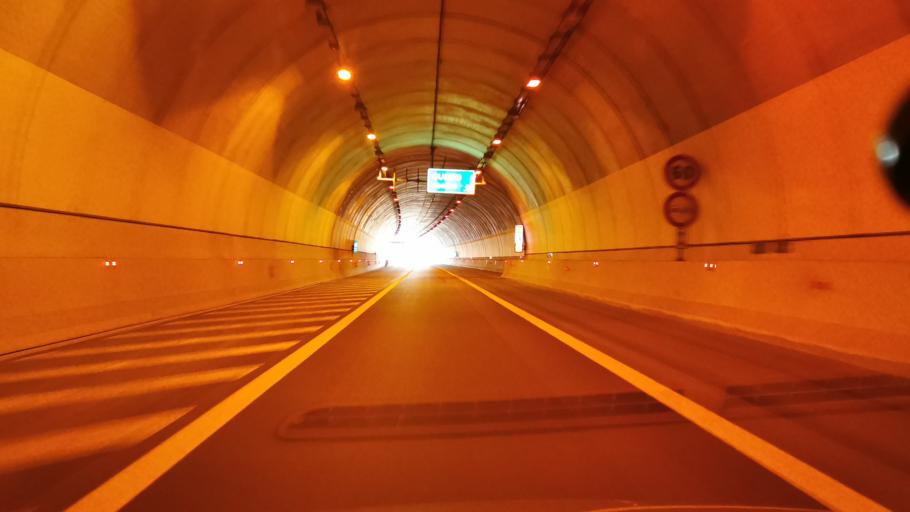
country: IT
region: Piedmont
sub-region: Provincia di Cuneo
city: Cuneo
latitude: 44.4280
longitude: 7.5662
